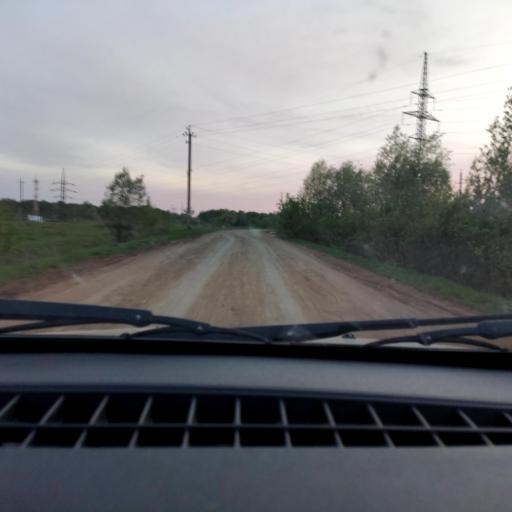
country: RU
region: Bashkortostan
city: Iglino
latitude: 54.8895
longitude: 56.3902
